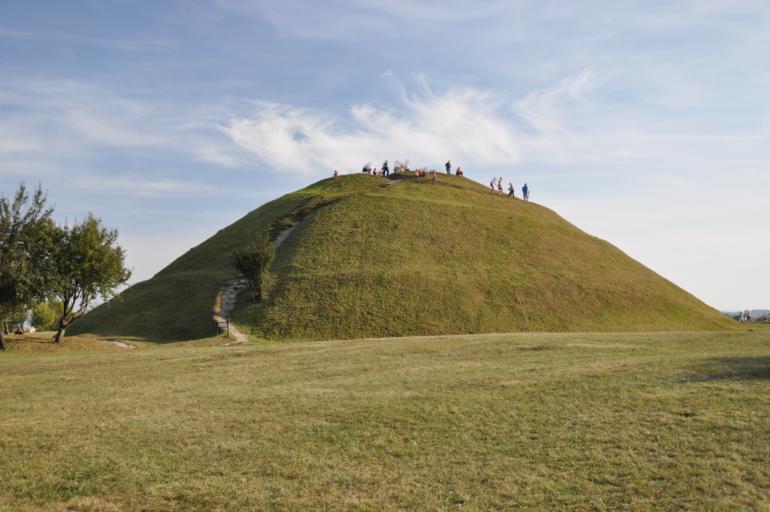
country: PL
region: Lesser Poland Voivodeship
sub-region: Krakow
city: Krakow
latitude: 50.0381
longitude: 19.9584
